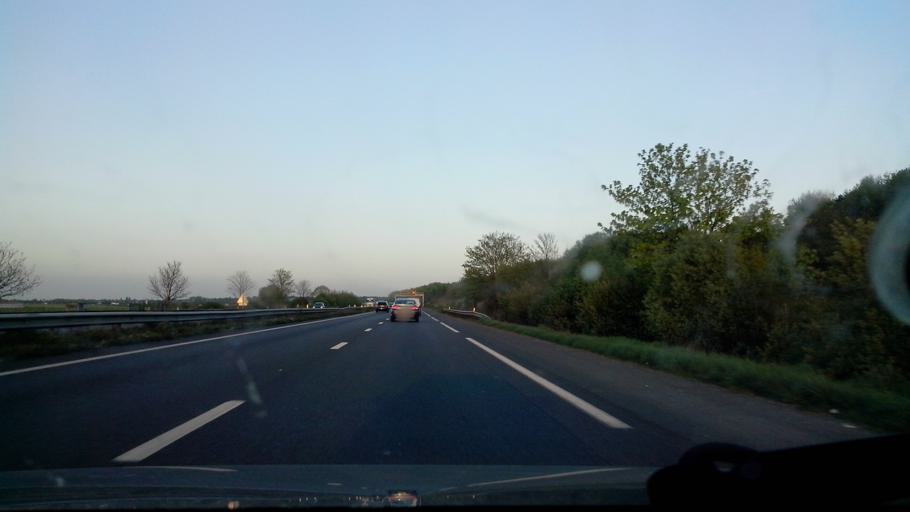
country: FR
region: Ile-de-France
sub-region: Departement de Seine-et-Marne
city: Moissy-Cramayel
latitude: 48.6464
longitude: 2.5919
